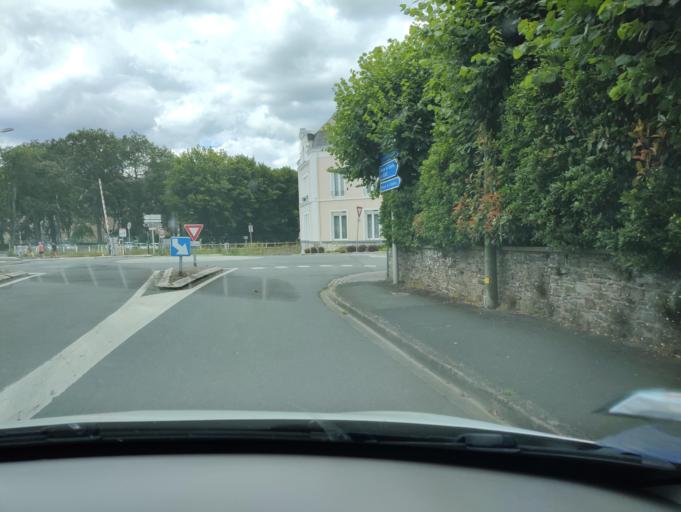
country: FR
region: Pays de la Loire
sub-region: Departement de la Loire-Atlantique
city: Chateaubriant
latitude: 47.7185
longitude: -1.3702
